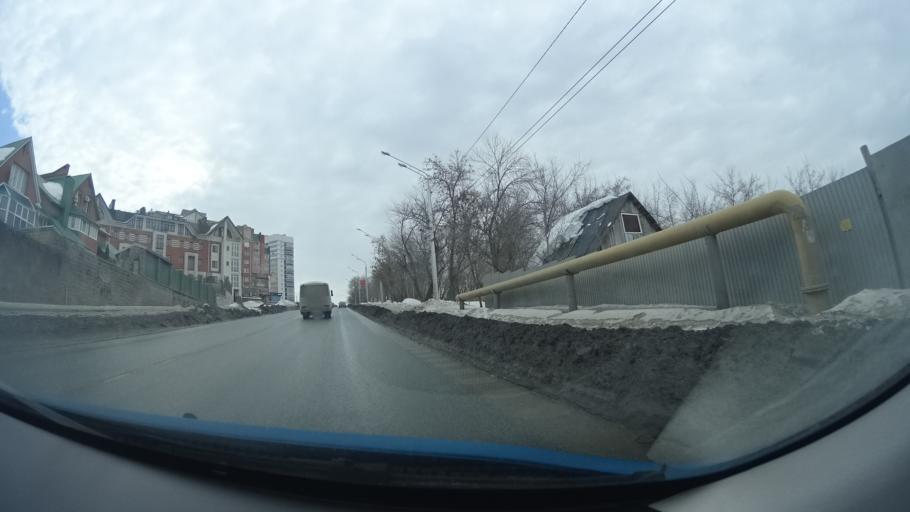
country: RU
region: Bashkortostan
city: Ufa
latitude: 54.7041
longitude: 55.9754
